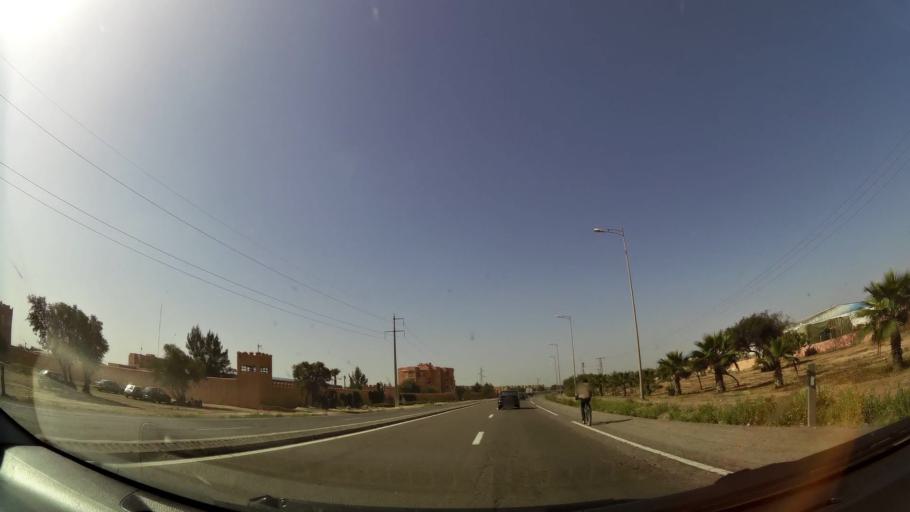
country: MA
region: Souss-Massa-Draa
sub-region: Inezgane-Ait Mellou
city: Inezgane
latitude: 30.3297
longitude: -9.4792
